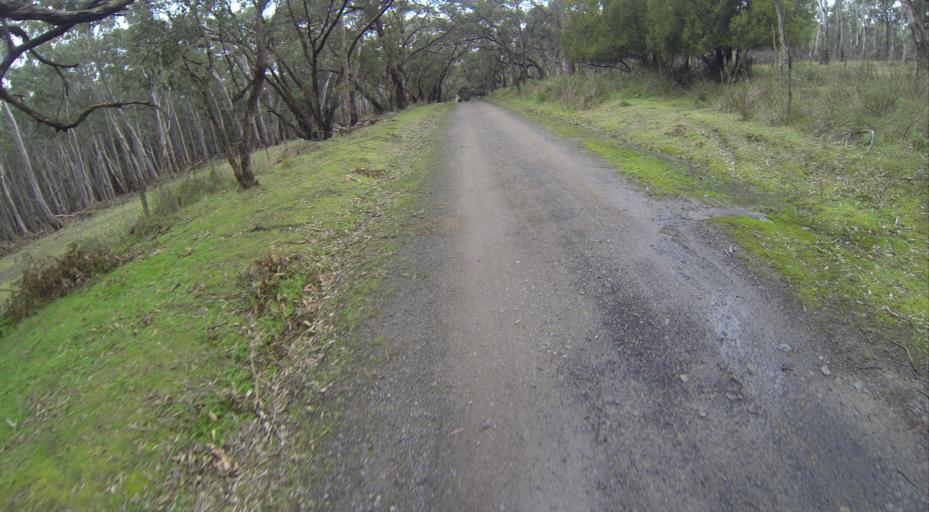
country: AU
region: Victoria
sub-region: Yarra Ranges
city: Lysterfield
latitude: -37.9494
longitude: 145.3087
